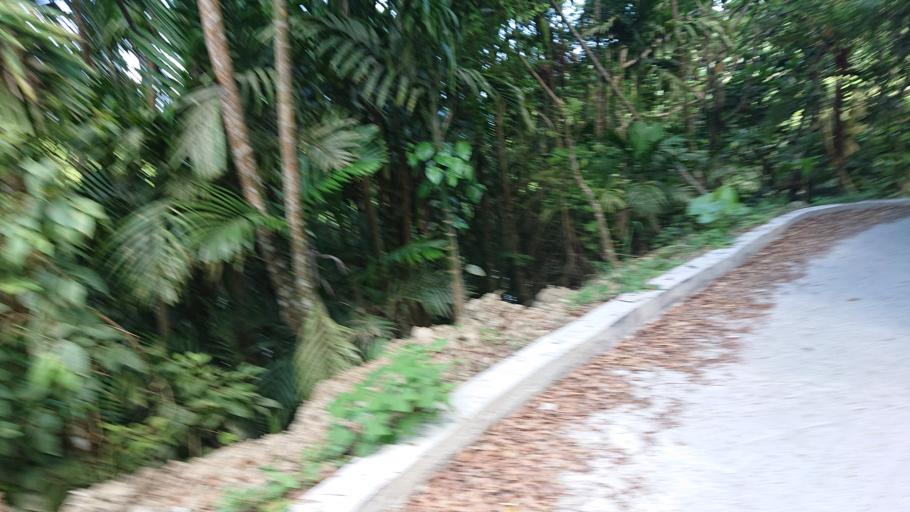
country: TW
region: Taiwan
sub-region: Hualien
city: Hualian
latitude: 23.7674
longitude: 121.5625
